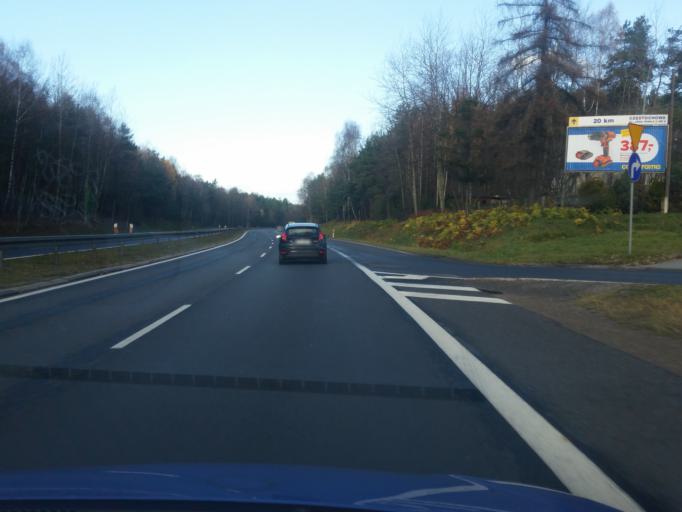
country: PL
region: Silesian Voivodeship
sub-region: Powiat czestochowski
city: Kamienica Polska
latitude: 50.6619
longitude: 19.1285
